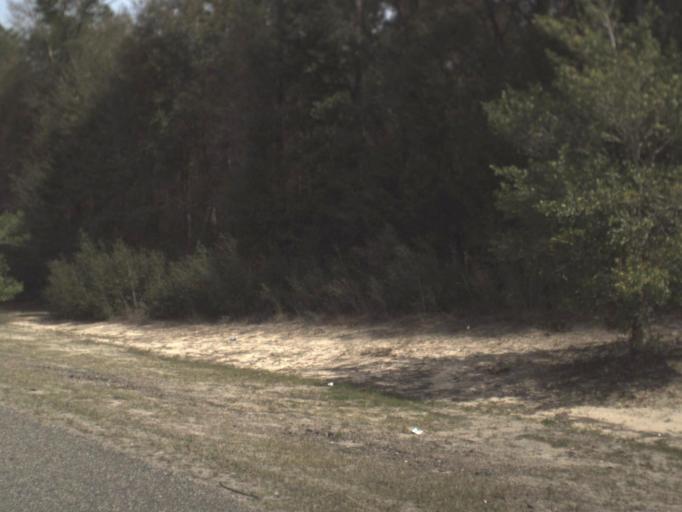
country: US
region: Florida
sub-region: Leon County
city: Tallahassee
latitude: 30.4085
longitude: -84.3530
